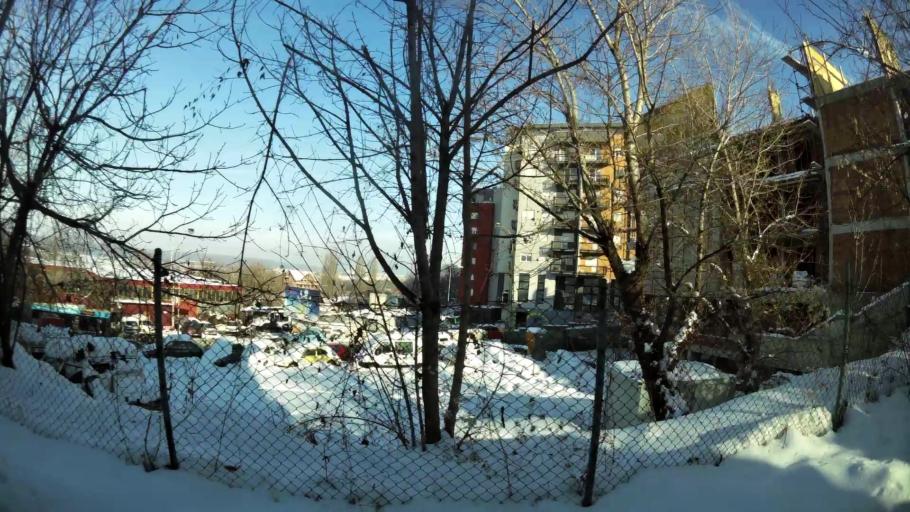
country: RS
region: Central Serbia
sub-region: Belgrade
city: Palilula
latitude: 44.8162
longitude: 20.5034
